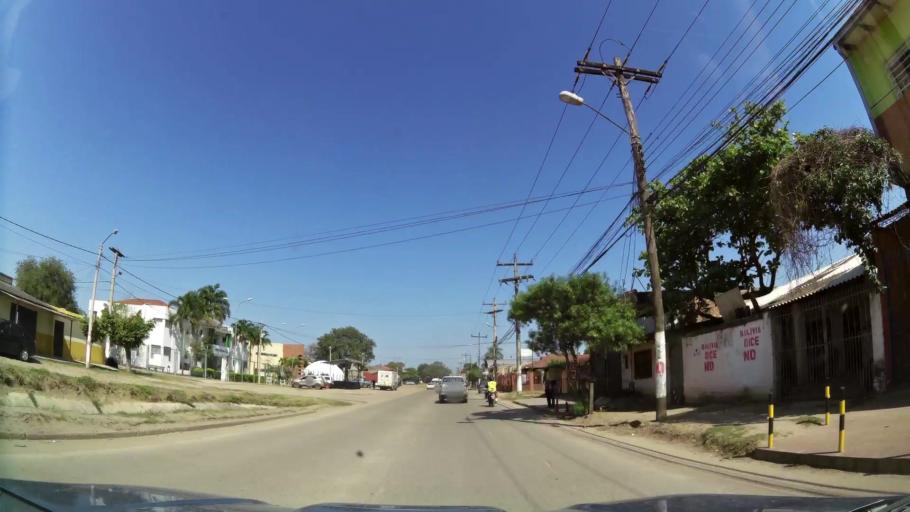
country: BO
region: Santa Cruz
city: Santa Cruz de la Sierra
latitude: -17.7486
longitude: -63.1222
